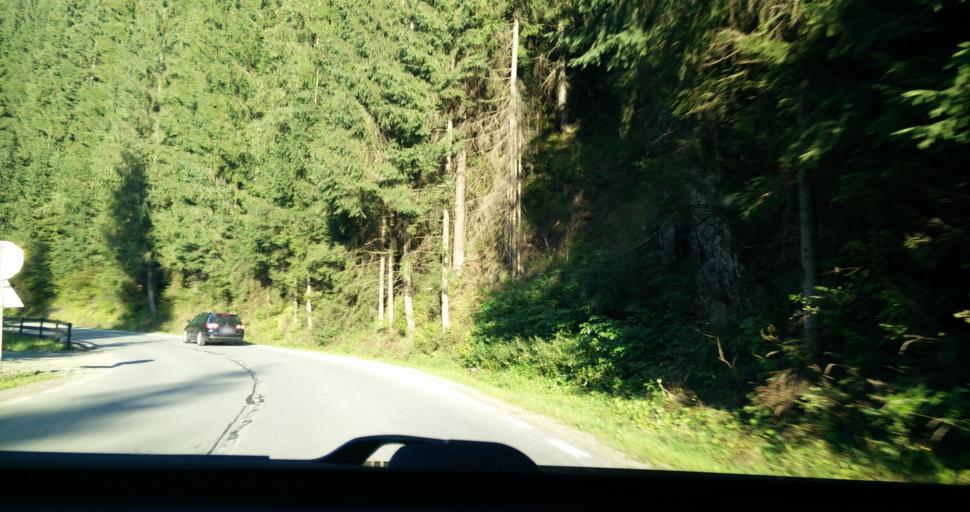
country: RO
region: Alba
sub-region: Comuna Arieseni
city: Arieseni
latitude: 46.4723
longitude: 22.7612
